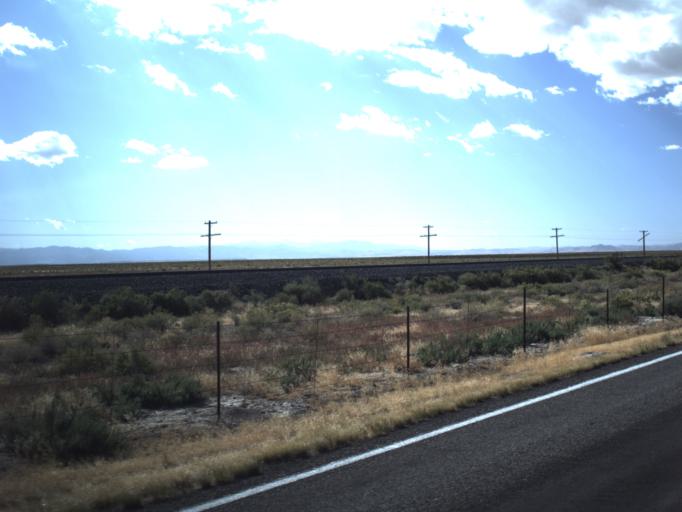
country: US
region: Utah
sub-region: Millard County
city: Delta
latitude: 39.0598
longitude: -112.7637
